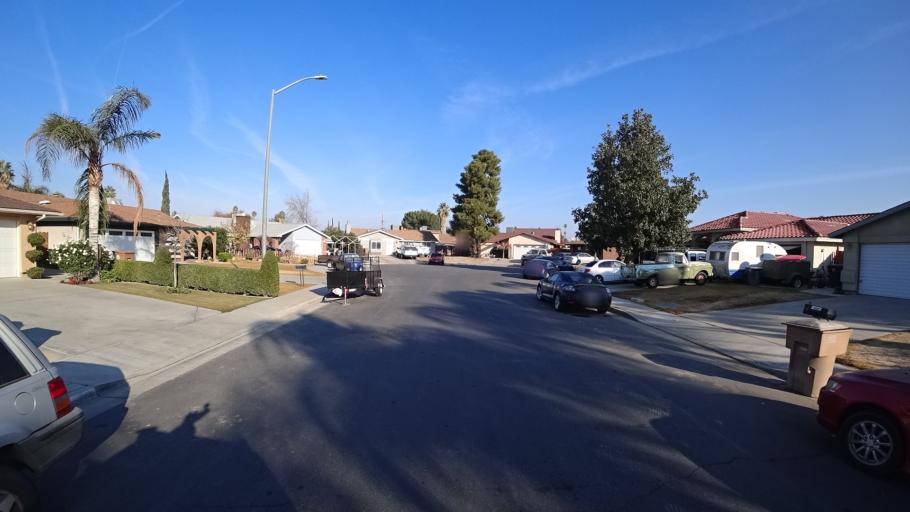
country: US
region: California
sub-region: Kern County
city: Greenfield
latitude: 35.3133
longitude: -119.0093
